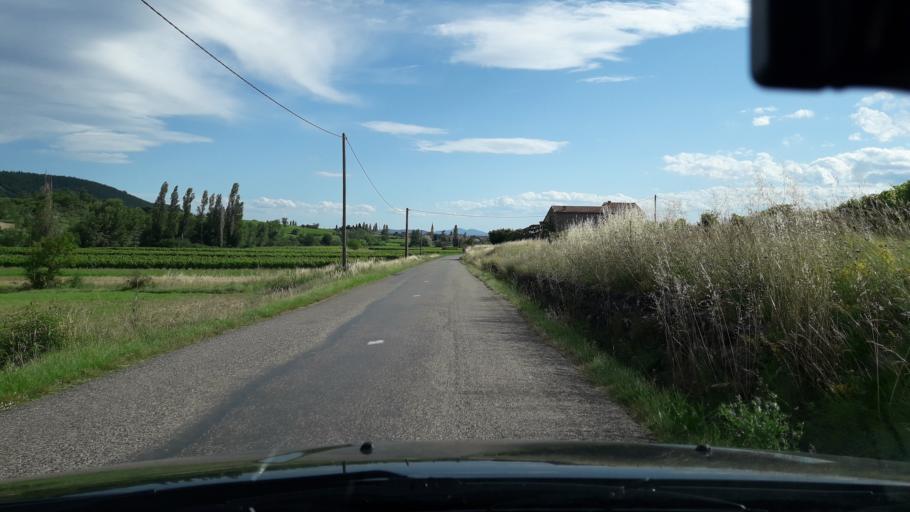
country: FR
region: Rhone-Alpes
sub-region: Departement de l'Ardeche
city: Vesseaux
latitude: 44.6217
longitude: 4.4797
